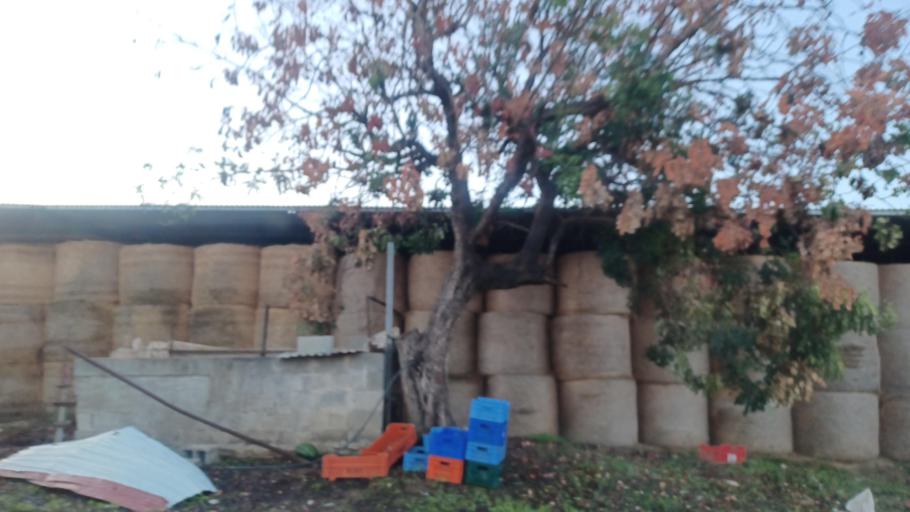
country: CY
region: Pafos
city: Polis
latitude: 34.9852
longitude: 32.4368
